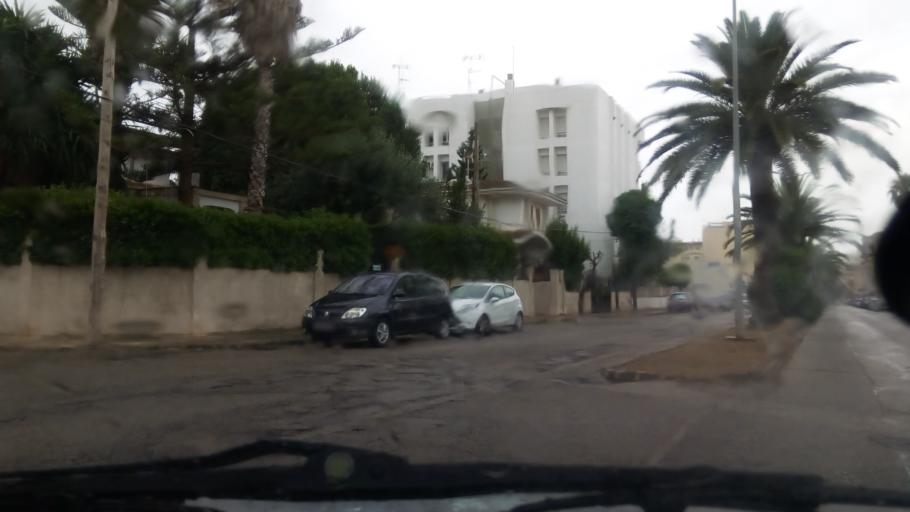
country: ES
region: Balearic Islands
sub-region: Illes Balears
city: Manacor
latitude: 39.5678
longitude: 3.2190
